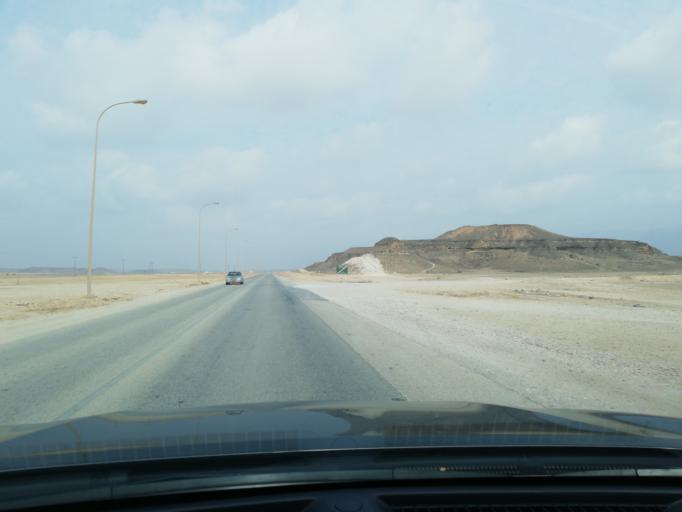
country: OM
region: Zufar
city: Salalah
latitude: 16.9518
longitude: 53.9291
